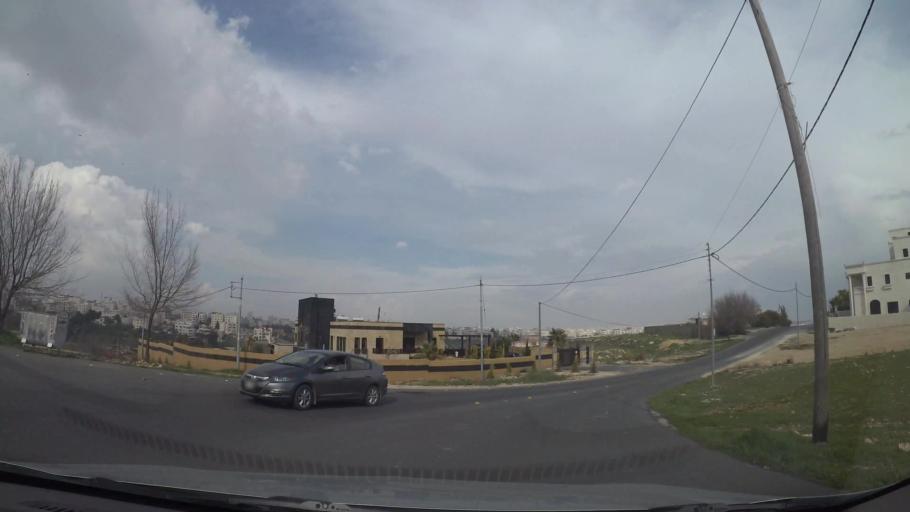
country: JO
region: Amman
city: Umm as Summaq
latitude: 31.8878
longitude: 35.8676
